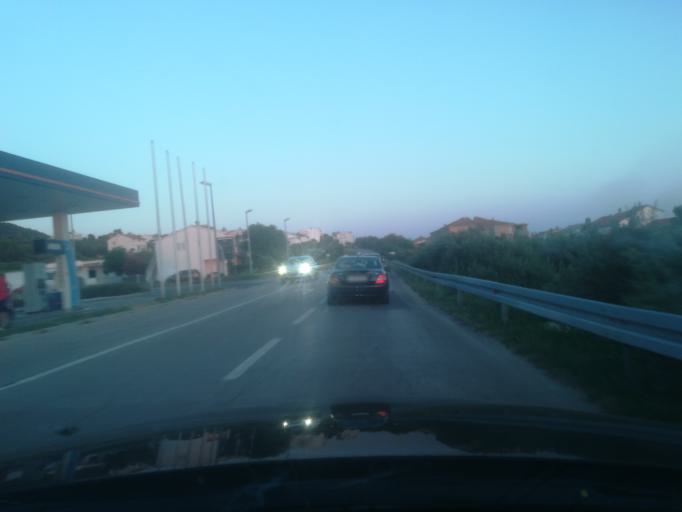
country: HR
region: Primorsko-Goranska
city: Banjol
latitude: 44.7478
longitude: 14.7889
